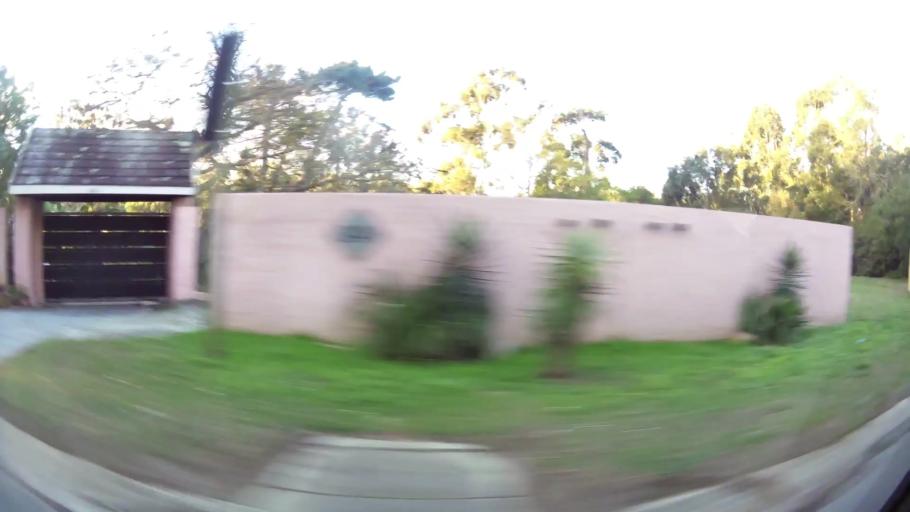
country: ZA
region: Eastern Cape
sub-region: Nelson Mandela Bay Metropolitan Municipality
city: Port Elizabeth
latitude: -33.9606
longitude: 25.5185
